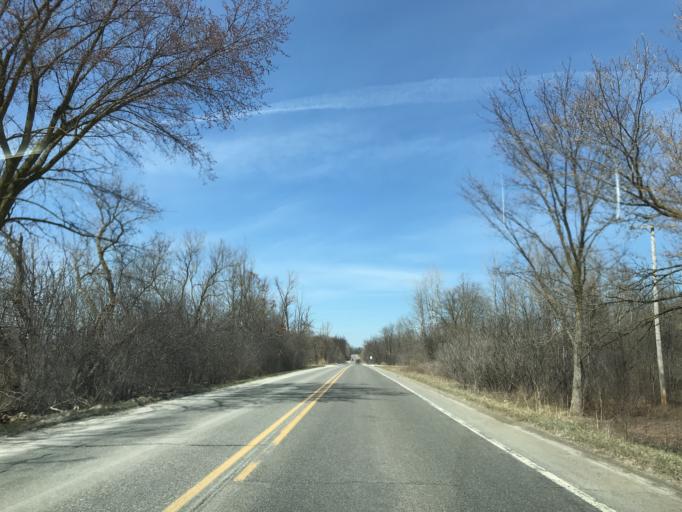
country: US
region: Michigan
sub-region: Washtenaw County
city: Ann Arbor
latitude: 42.3304
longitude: -83.7081
